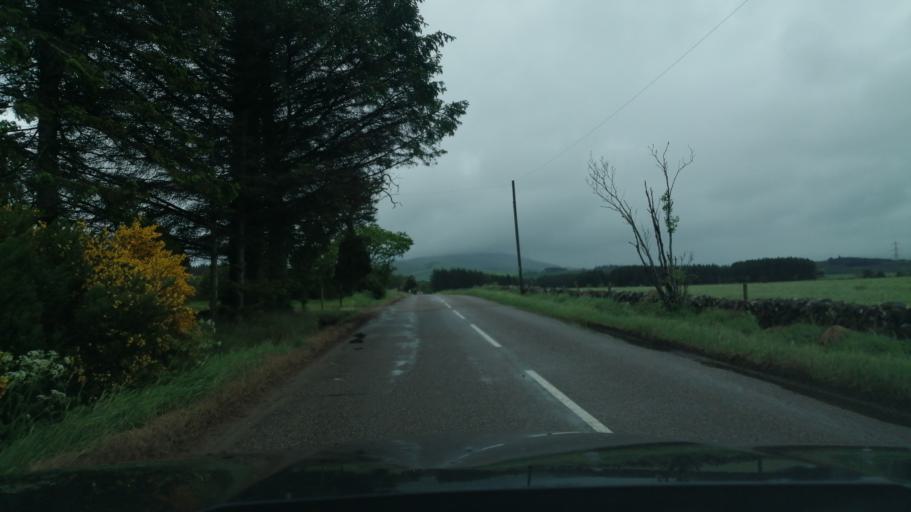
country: GB
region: Scotland
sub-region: Aberdeenshire
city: Huntly
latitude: 57.5367
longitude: -2.7732
